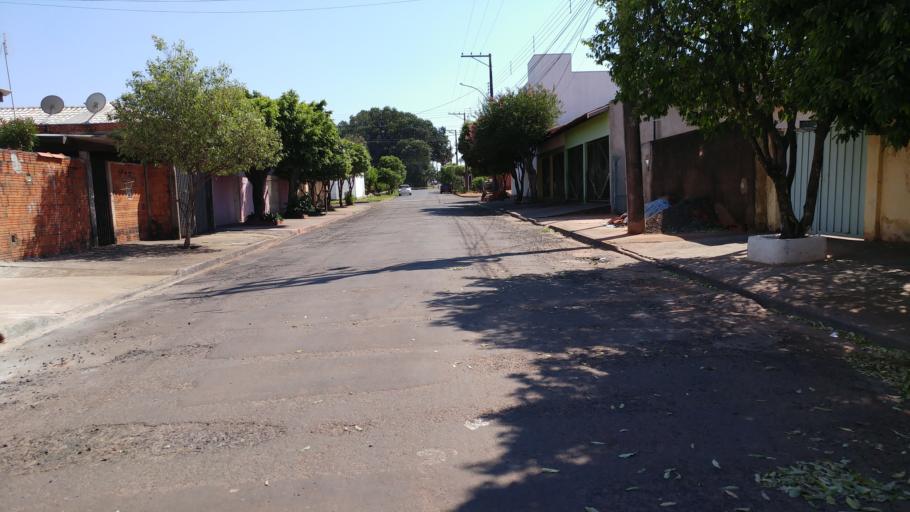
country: BR
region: Sao Paulo
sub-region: Paraguacu Paulista
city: Paraguacu Paulista
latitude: -22.4193
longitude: -50.5881
